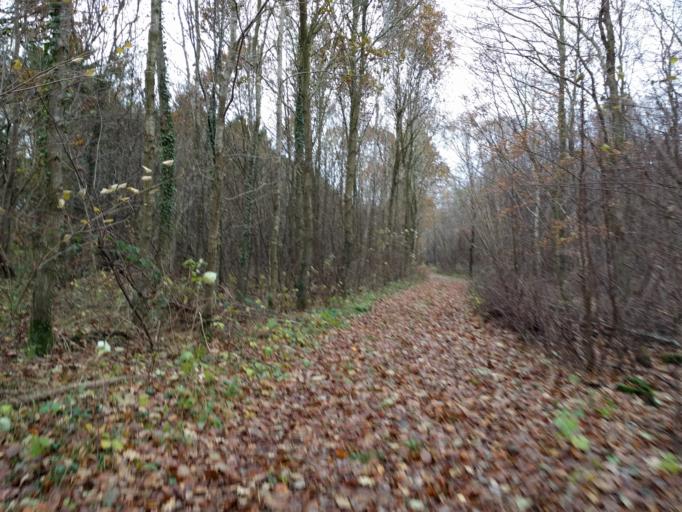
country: DK
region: South Denmark
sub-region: Kerteminde Kommune
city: Langeskov
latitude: 55.4025
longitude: 10.5668
